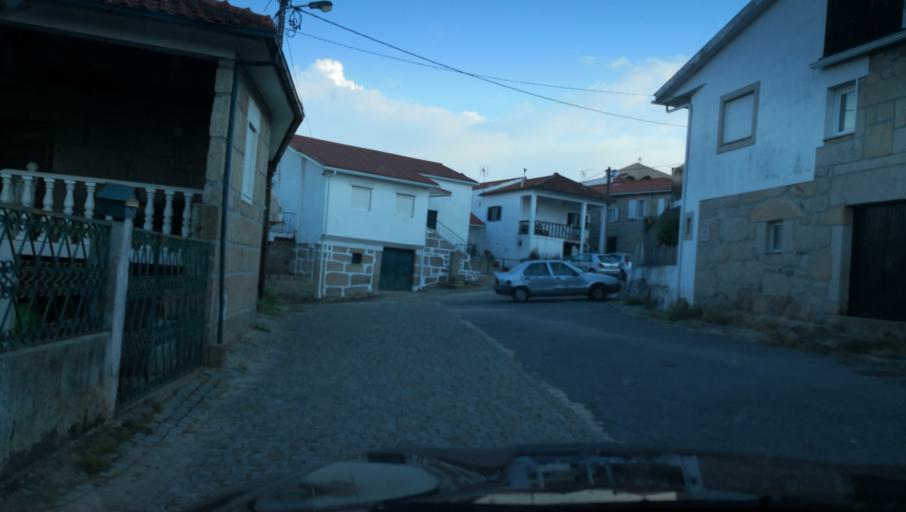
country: PT
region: Vila Real
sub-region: Santa Marta de Penaguiao
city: Santa Marta de Penaguiao
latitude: 41.2622
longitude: -7.7908
